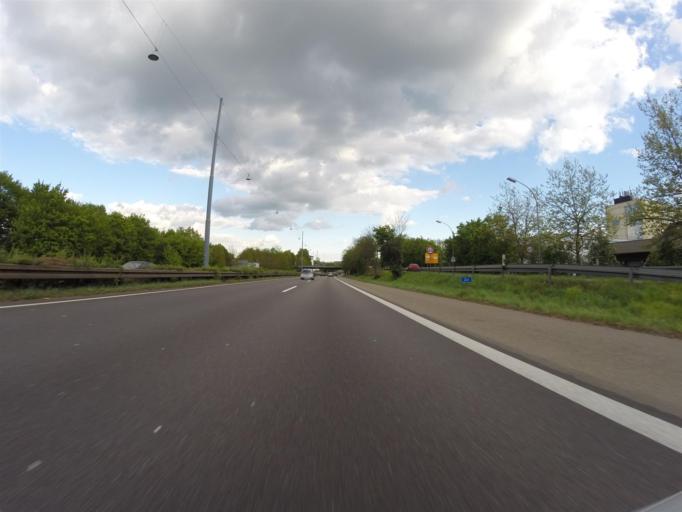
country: DE
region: Saarland
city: Saarbrucken
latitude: 49.2221
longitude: 7.0128
